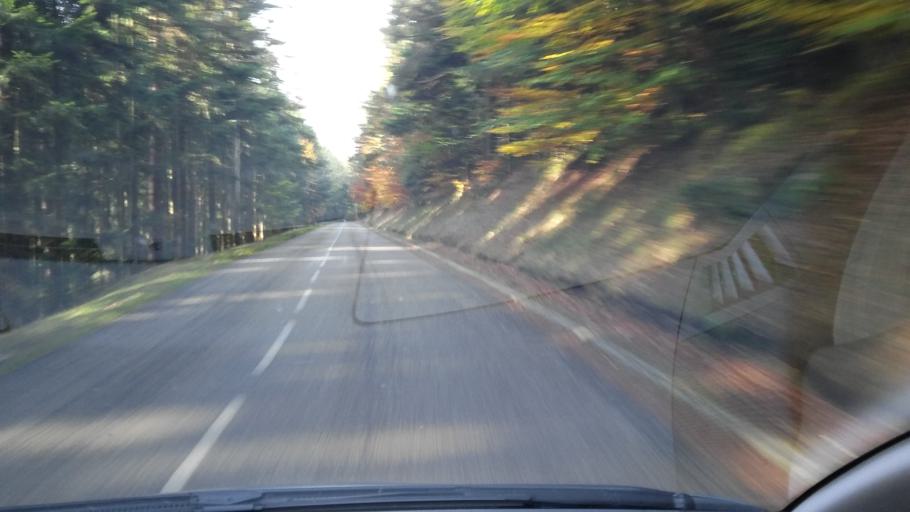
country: FR
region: Lorraine
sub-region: Departement de la Moselle
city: Dabo
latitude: 48.6641
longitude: 7.2618
